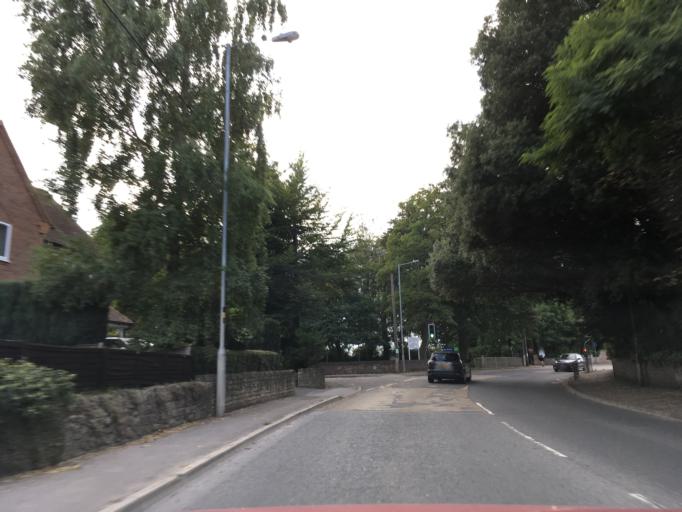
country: GB
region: England
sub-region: Wiltshire
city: Devizes
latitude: 51.3472
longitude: -1.9831
